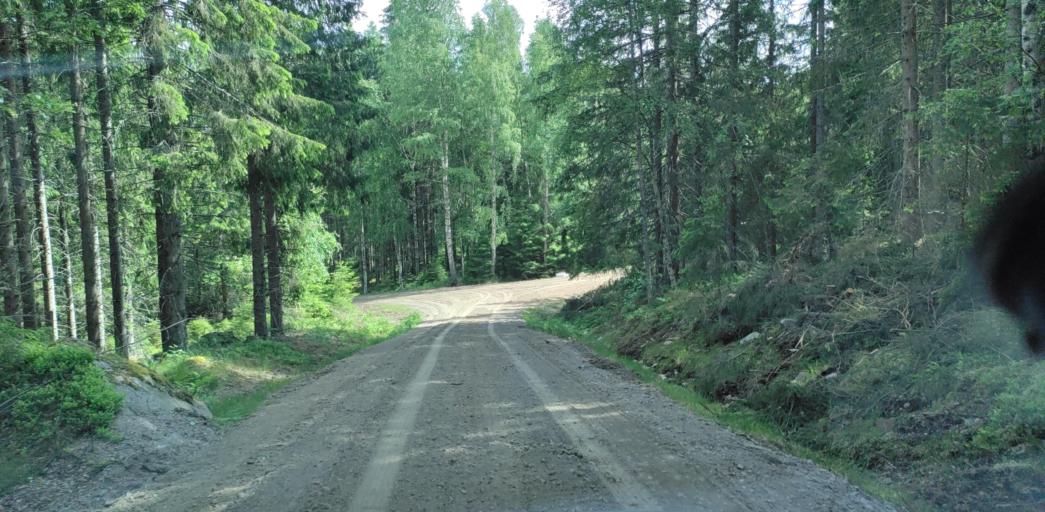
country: SE
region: Vaermland
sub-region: Munkfors Kommun
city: Munkfors
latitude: 59.9691
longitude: 13.4029
